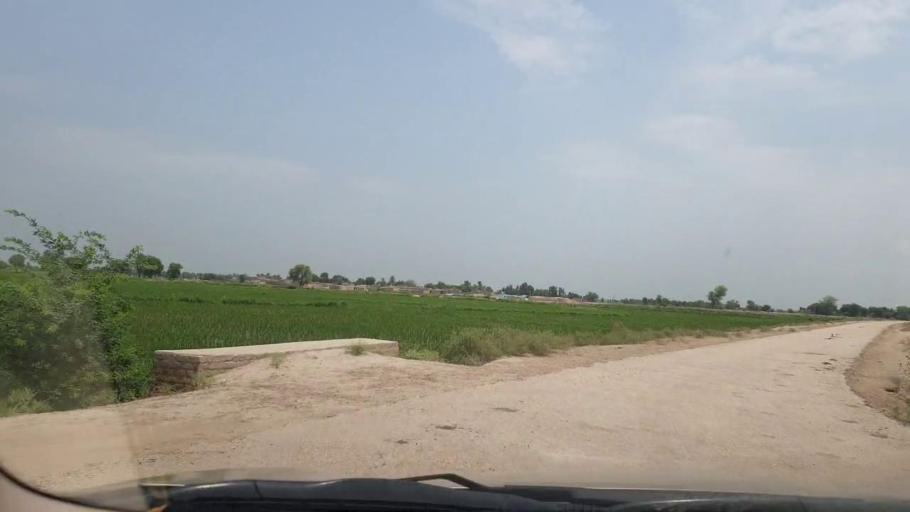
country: PK
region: Sindh
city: Larkana
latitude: 27.6089
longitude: 68.1447
